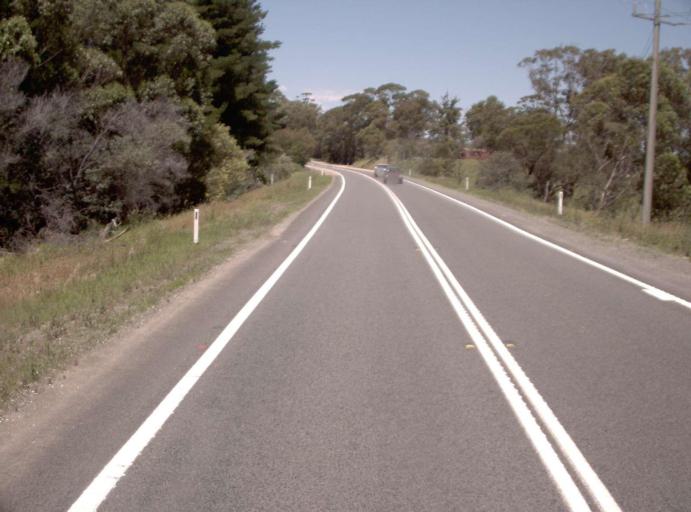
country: AU
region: Victoria
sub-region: East Gippsland
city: Lakes Entrance
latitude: -37.7031
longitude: 148.5655
